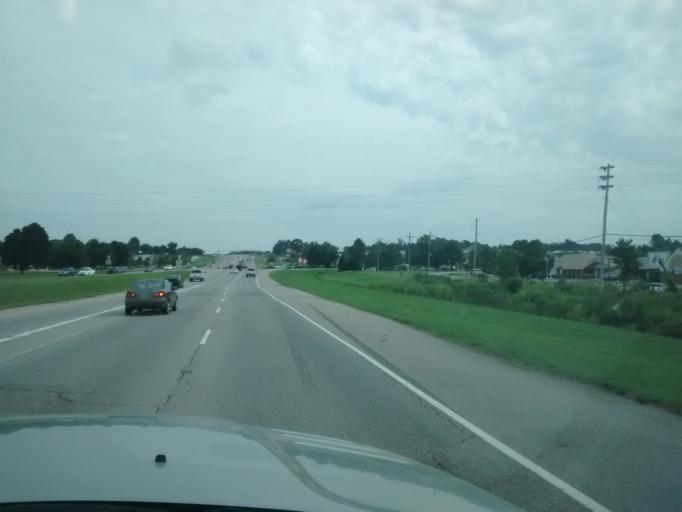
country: US
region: Arkansas
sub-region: Washington County
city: Johnson
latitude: 36.1197
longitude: -94.1448
